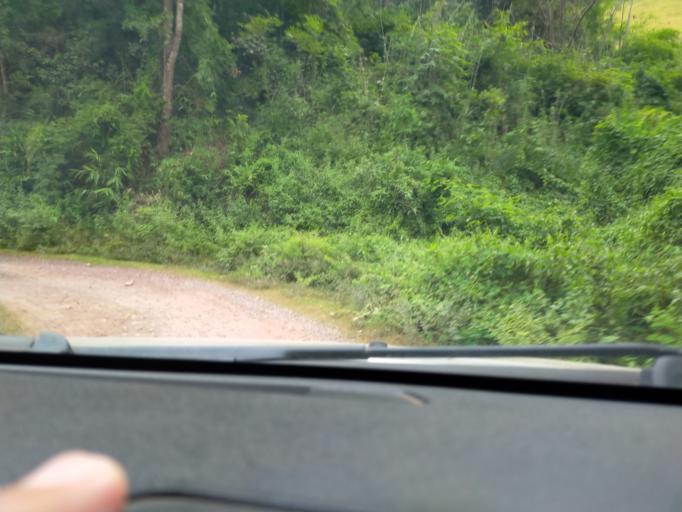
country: TH
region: Nan
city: Chaloem Phra Kiat
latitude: 19.7895
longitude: 101.3608
